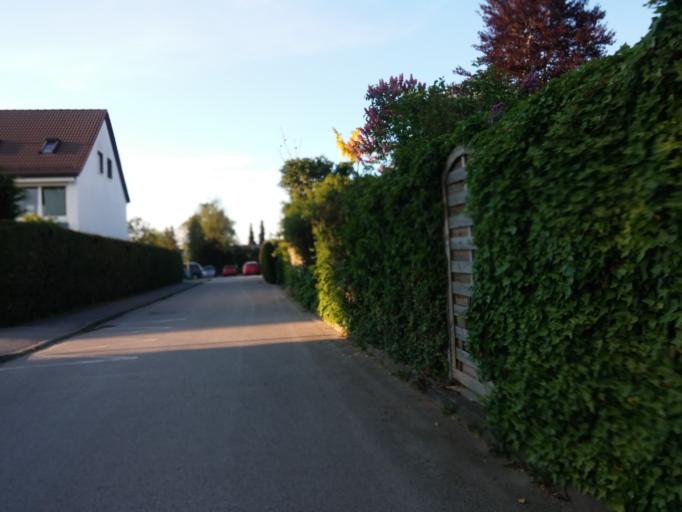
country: DE
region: Bavaria
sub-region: Upper Bavaria
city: Vaterstetten
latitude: 48.1055
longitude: 11.7894
